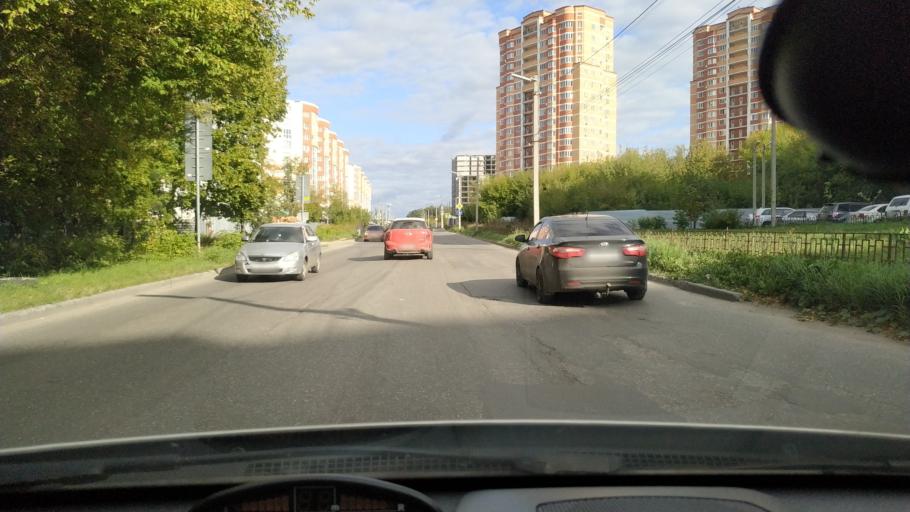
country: RU
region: Rjazan
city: Ryazan'
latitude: 54.6051
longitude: 39.7358
